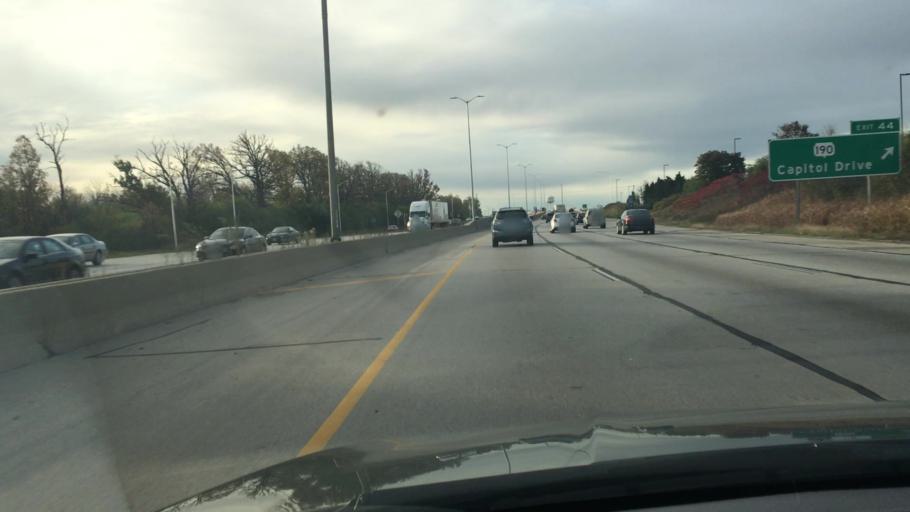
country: US
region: Wisconsin
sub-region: Waukesha County
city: Butler
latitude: 43.0941
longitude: -88.0582
